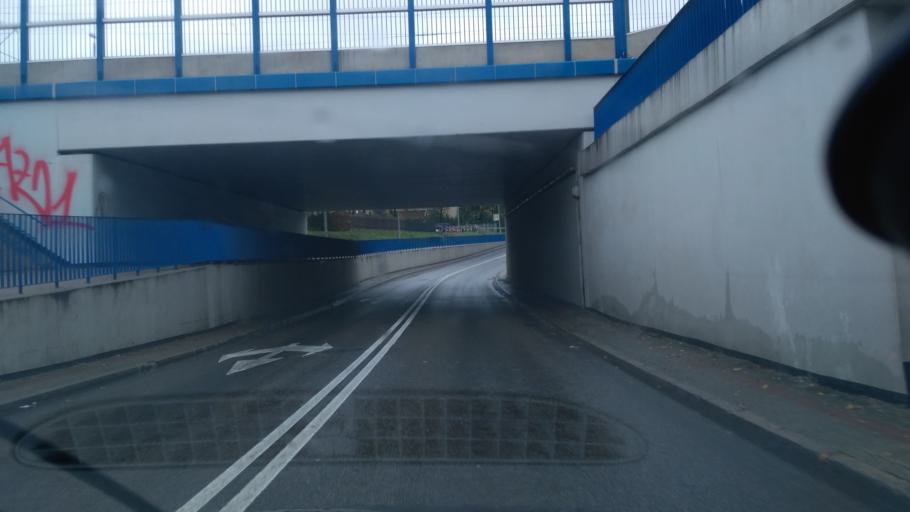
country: PL
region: Subcarpathian Voivodeship
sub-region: Powiat debicki
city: Debica
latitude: 50.0562
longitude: 21.4092
